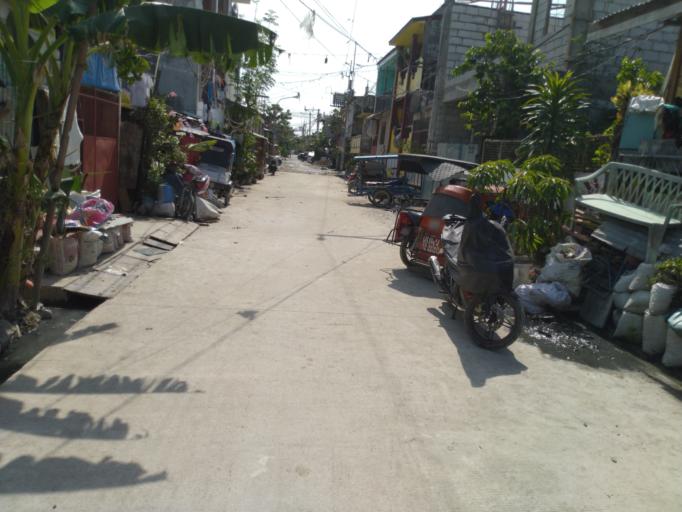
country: PH
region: Calabarzon
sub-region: Province of Rizal
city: Taytay
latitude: 14.5357
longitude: 121.1108
